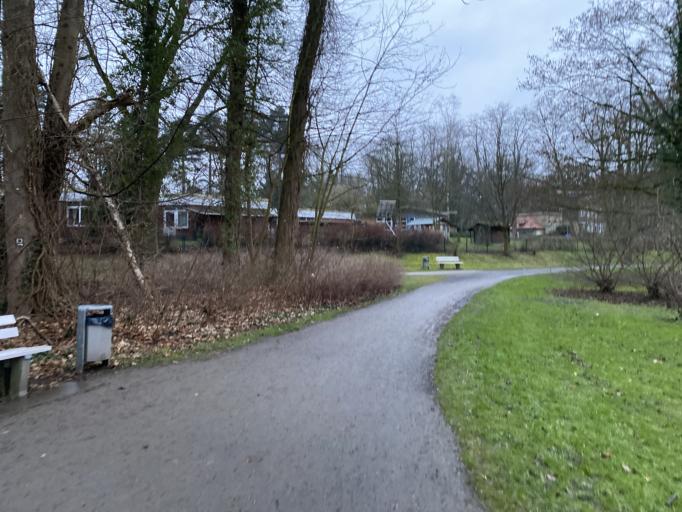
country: DE
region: North Rhine-Westphalia
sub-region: Regierungsbezirk Arnsberg
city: Hamm
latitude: 51.6930
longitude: 7.8499
